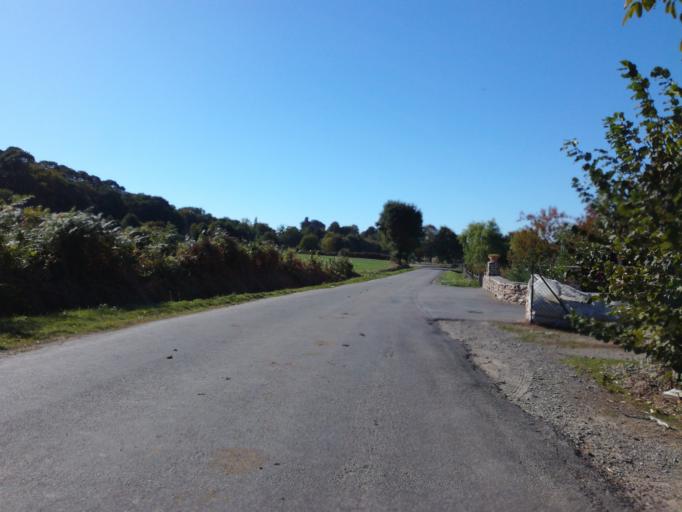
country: FR
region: Brittany
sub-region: Departement d'Ille-et-Vilaine
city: Saint-Aubin-du-Cormier
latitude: 48.2620
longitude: -1.3861
